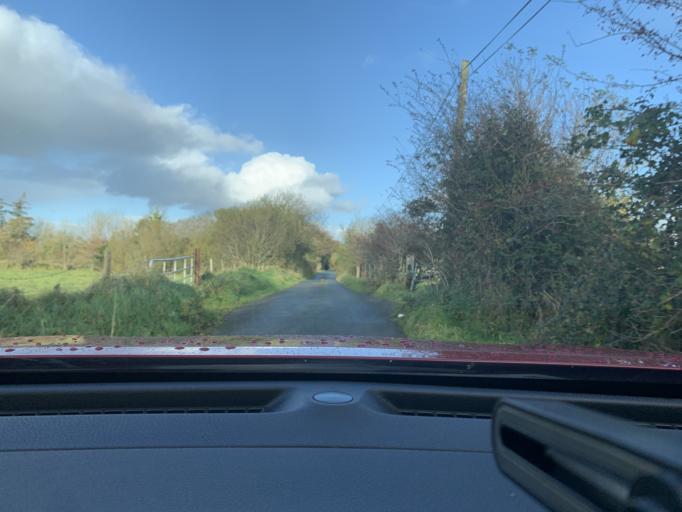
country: IE
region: Connaught
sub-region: Sligo
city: Ballymote
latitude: 54.0966
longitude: -8.4374
